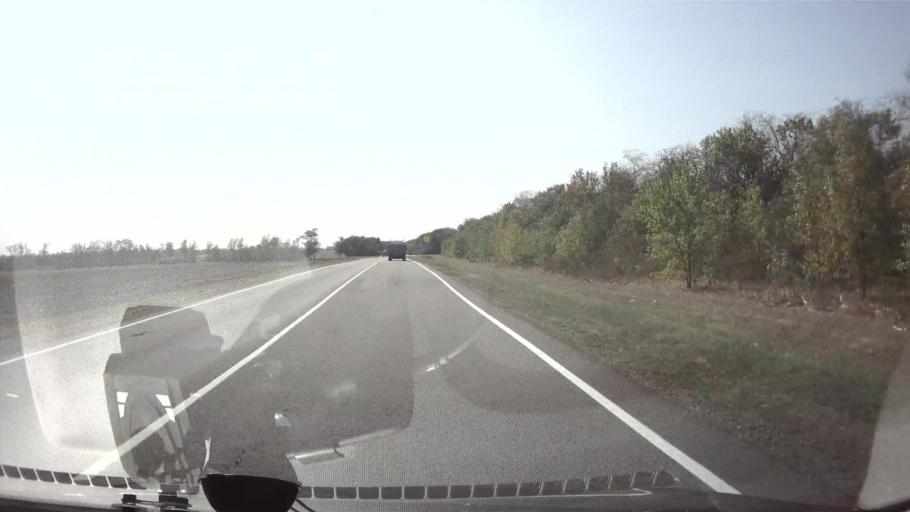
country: RU
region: Krasnodarskiy
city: Novopokrovskaya
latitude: 45.8207
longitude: 40.7201
